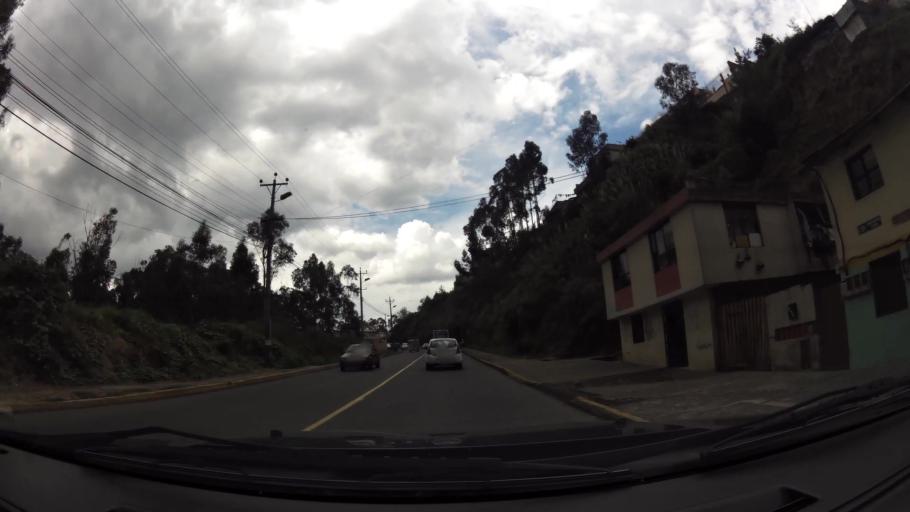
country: EC
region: Pichincha
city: Quito
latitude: -0.2427
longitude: -78.5006
